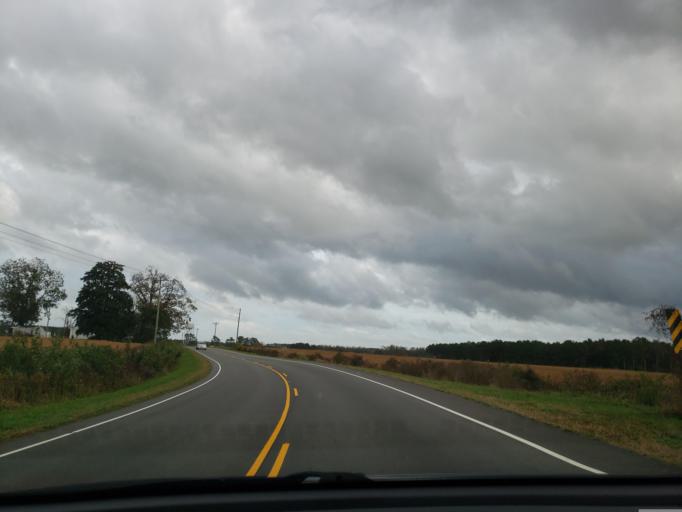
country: US
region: North Carolina
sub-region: Duplin County
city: Kenansville
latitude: 34.8887
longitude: -77.9050
